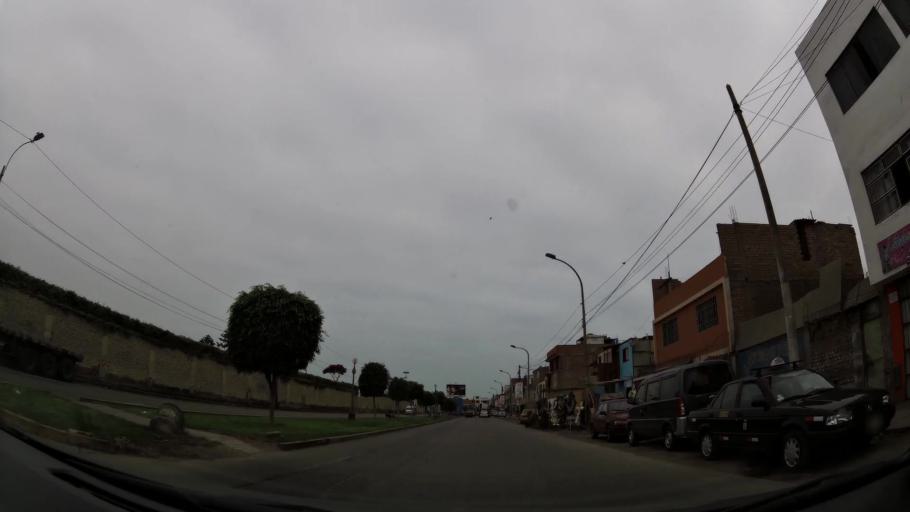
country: PE
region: Callao
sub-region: Callao
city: Callao
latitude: -12.0564
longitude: -77.1219
